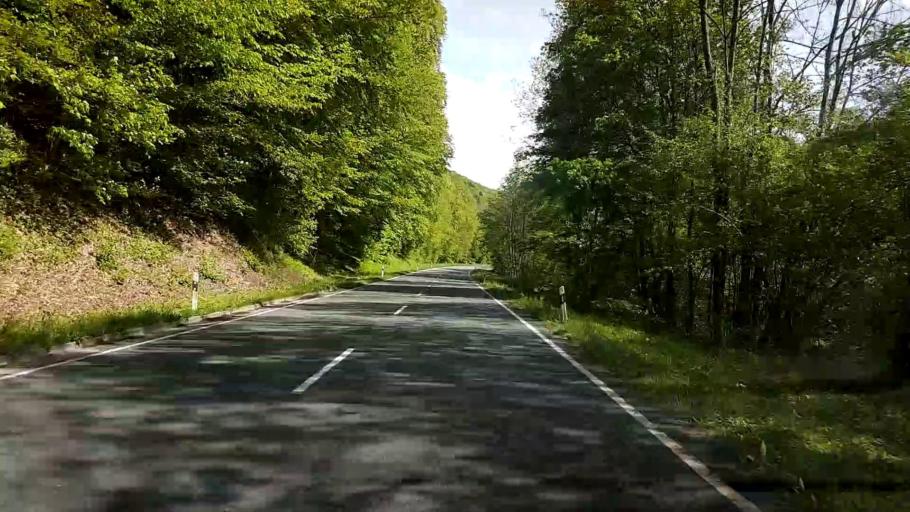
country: DE
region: Bavaria
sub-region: Upper Franconia
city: Ebermannstadt
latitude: 49.7998
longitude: 11.1699
